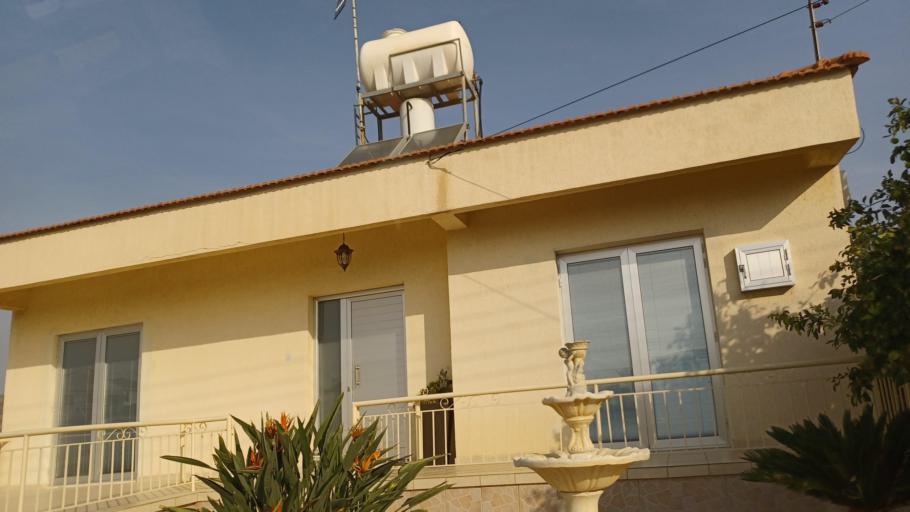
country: CY
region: Larnaka
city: Troulloi
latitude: 35.0337
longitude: 33.6125
